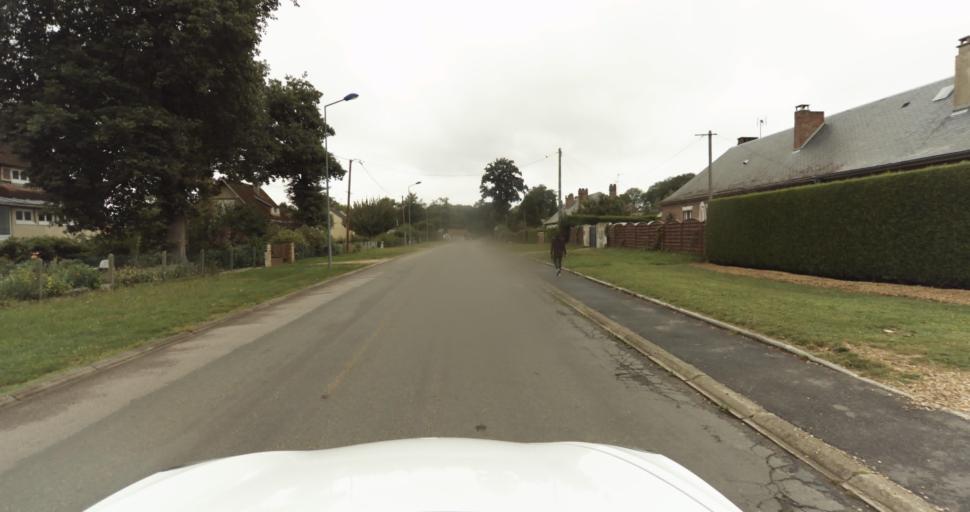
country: FR
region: Haute-Normandie
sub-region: Departement de l'Eure
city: Evreux
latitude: 49.0328
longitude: 1.1312
